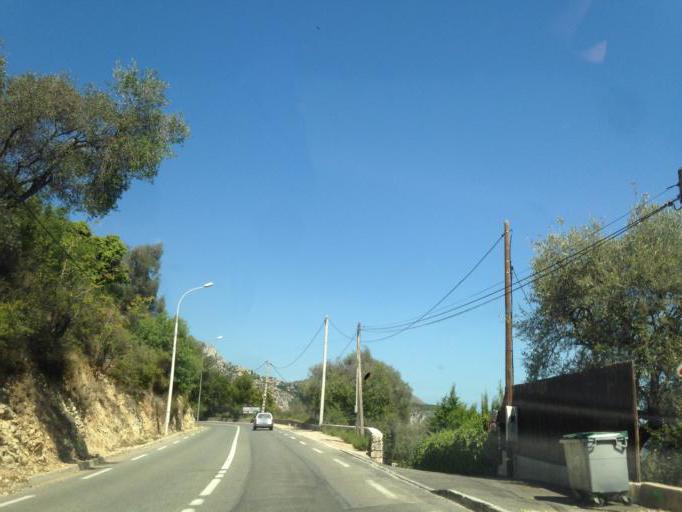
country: FR
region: Provence-Alpes-Cote d'Azur
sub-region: Departement des Alpes-Maritimes
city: Beaulieu-sur-Mer
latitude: 43.7188
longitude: 7.3373
